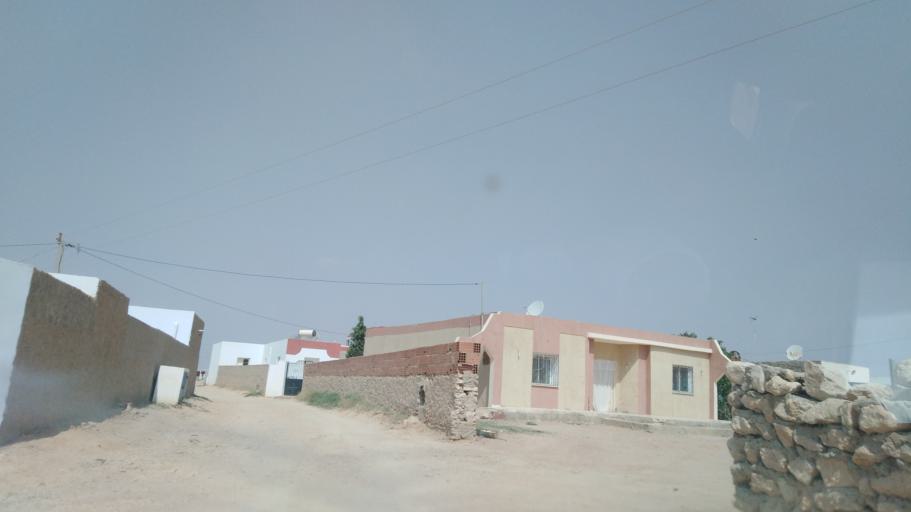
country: TN
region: Safaqis
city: Sfax
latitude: 34.6260
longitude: 10.5751
